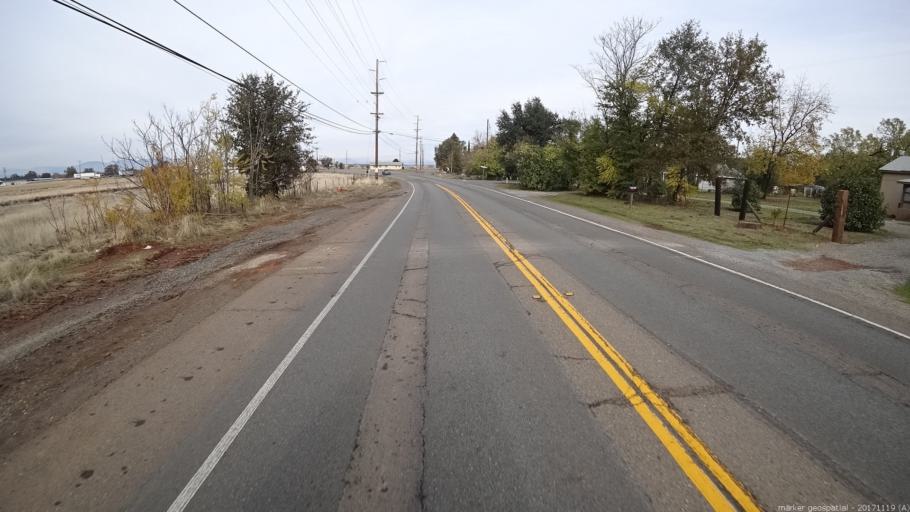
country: US
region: California
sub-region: Shasta County
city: Anderson
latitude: 40.4878
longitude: -122.2934
